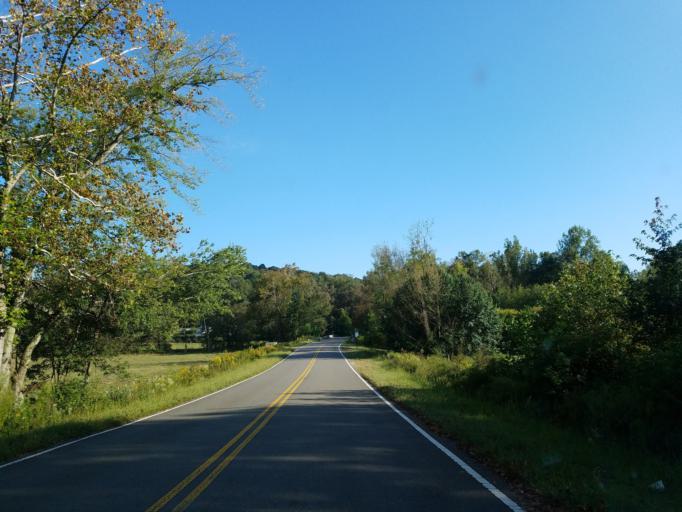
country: US
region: Georgia
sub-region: Gilmer County
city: Ellijay
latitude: 34.6627
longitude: -84.3828
